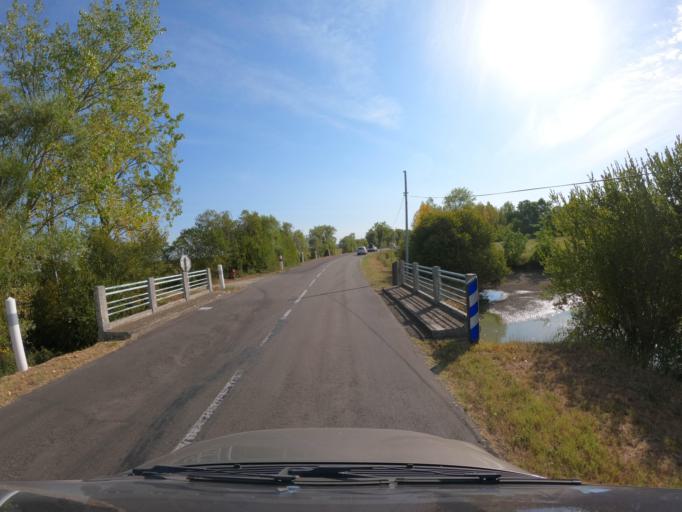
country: FR
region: Pays de la Loire
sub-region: Departement de la Vendee
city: Le Perrier
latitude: 46.8056
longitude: -1.9488
